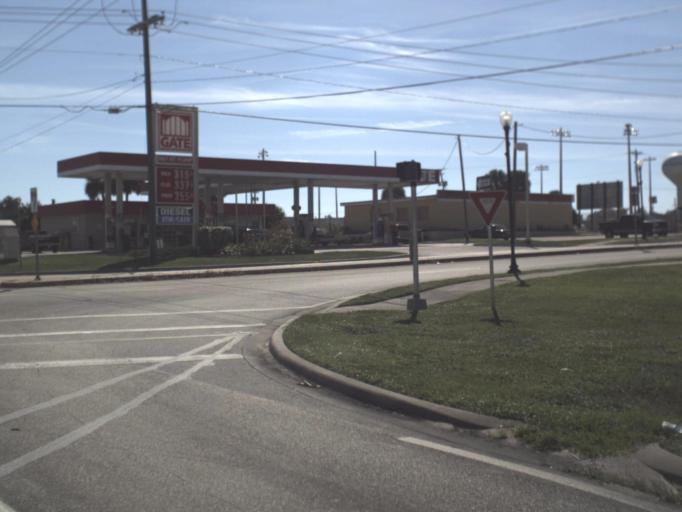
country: US
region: Florida
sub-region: Highlands County
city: Lake Placid
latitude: 27.3002
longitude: -81.3587
